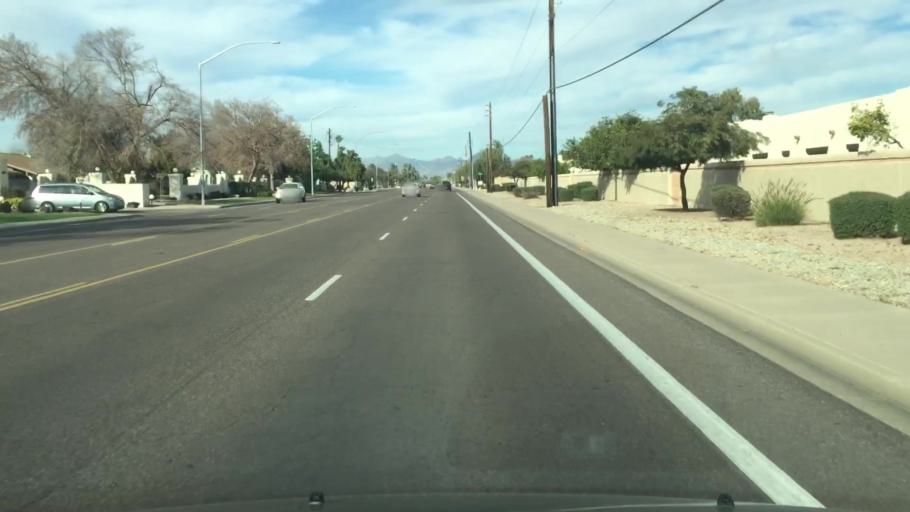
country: US
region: Arizona
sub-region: Maricopa County
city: Mesa
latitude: 33.4427
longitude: -111.8051
